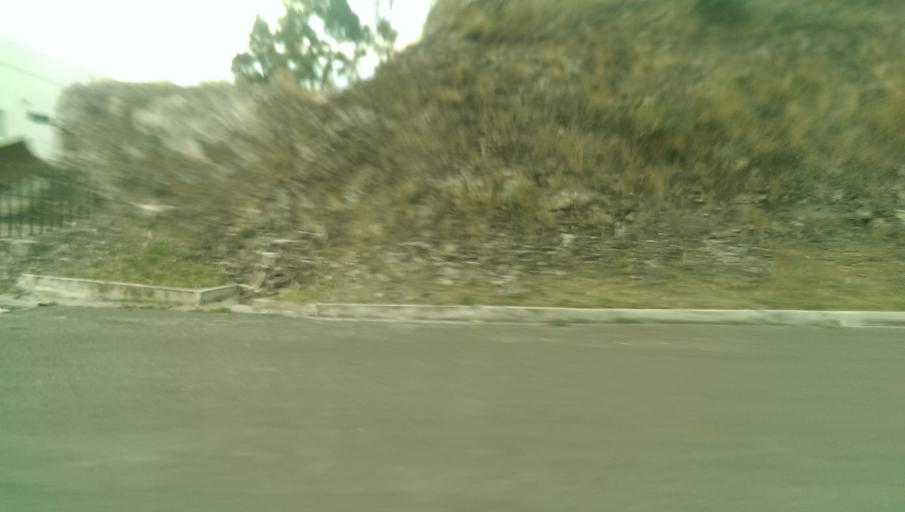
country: MX
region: Queretaro
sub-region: Queretaro
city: Santiago de Queretaro
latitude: 20.5838
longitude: -100.3569
